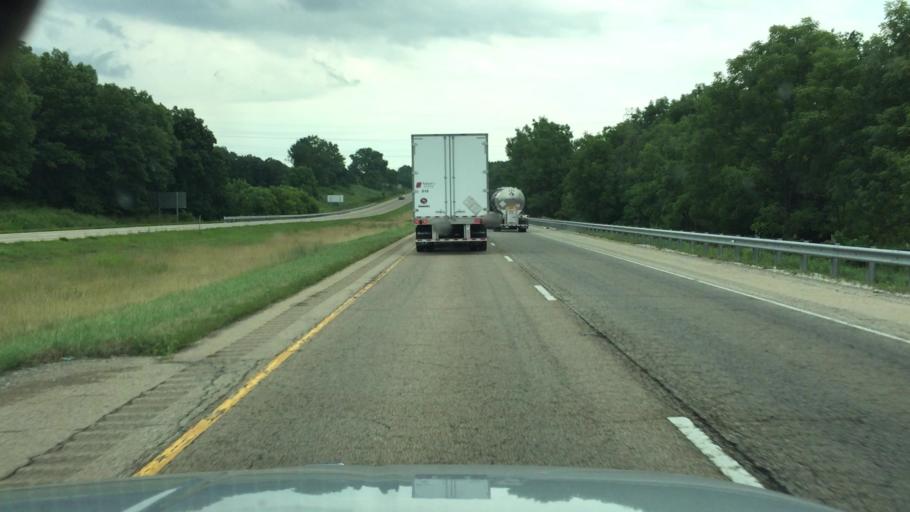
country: US
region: Illinois
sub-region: Peoria County
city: Hanna City
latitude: 40.7690
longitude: -89.7403
